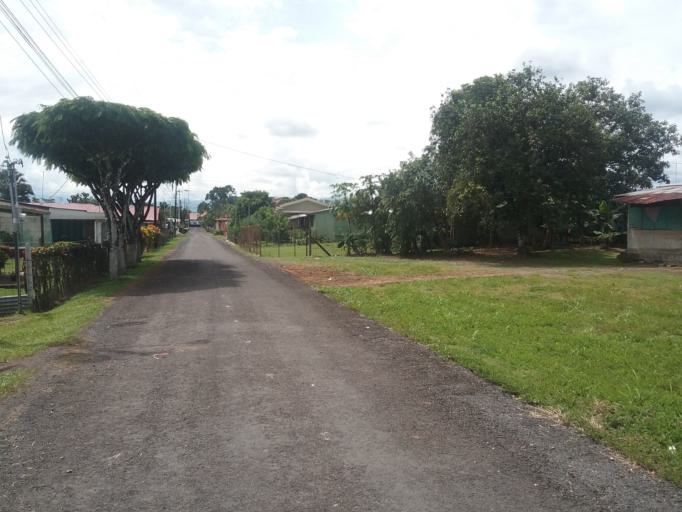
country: CR
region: Limon
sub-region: Canton de Pococi
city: Roxana
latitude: 10.3247
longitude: -83.8862
